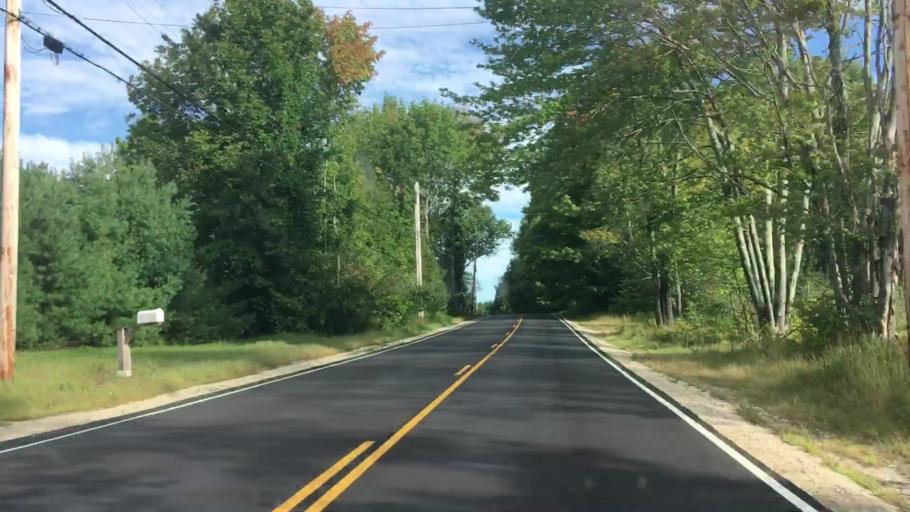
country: US
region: Maine
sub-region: Cumberland County
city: Cumberland Center
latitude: 43.7764
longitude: -70.3024
